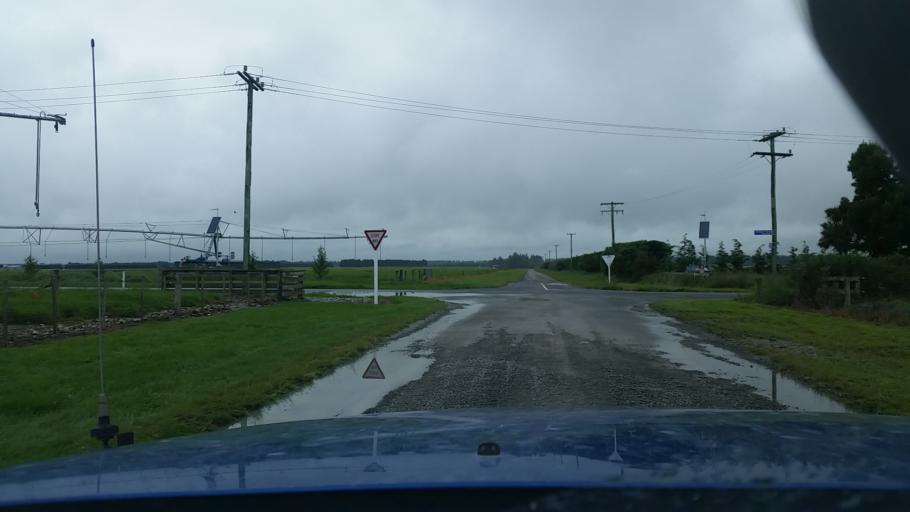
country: NZ
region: Canterbury
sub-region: Ashburton District
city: Methven
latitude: -43.7349
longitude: 171.6236
